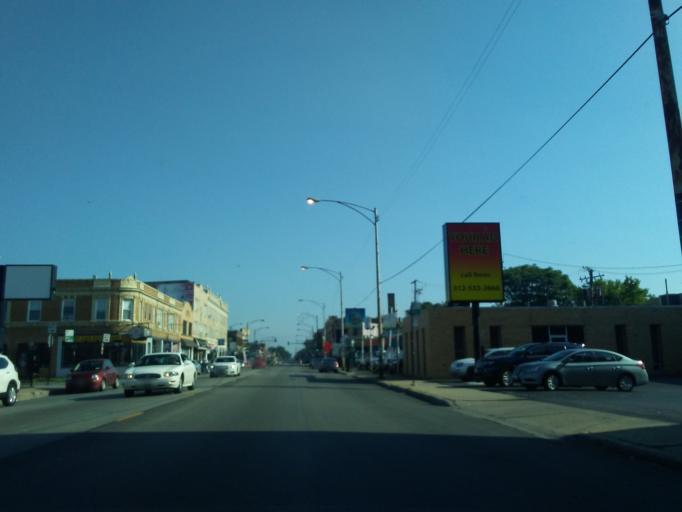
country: US
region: Illinois
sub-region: Cook County
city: Lincolnwood
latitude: 41.9396
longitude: -87.7271
